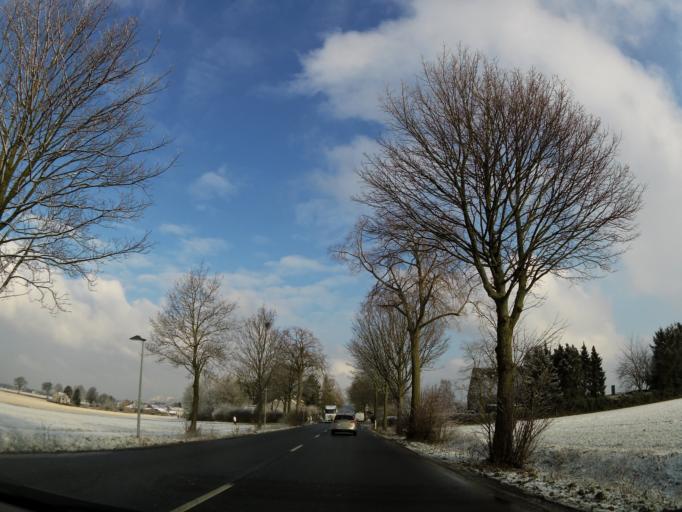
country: DE
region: North Rhine-Westphalia
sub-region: Regierungsbezirk Koln
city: Wurselen
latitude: 50.8374
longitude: 6.1337
